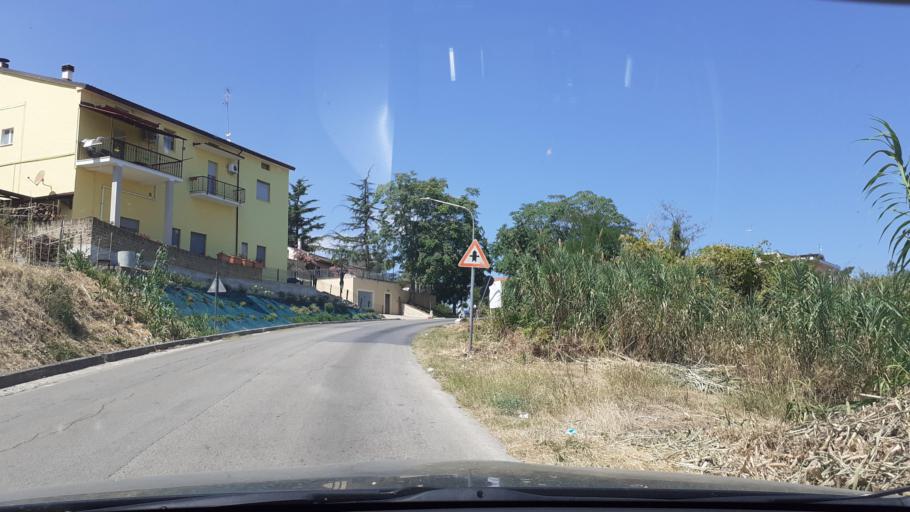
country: IT
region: Abruzzo
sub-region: Provincia di Chieti
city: Santa Maria Imbaro
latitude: 42.2198
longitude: 14.4516
